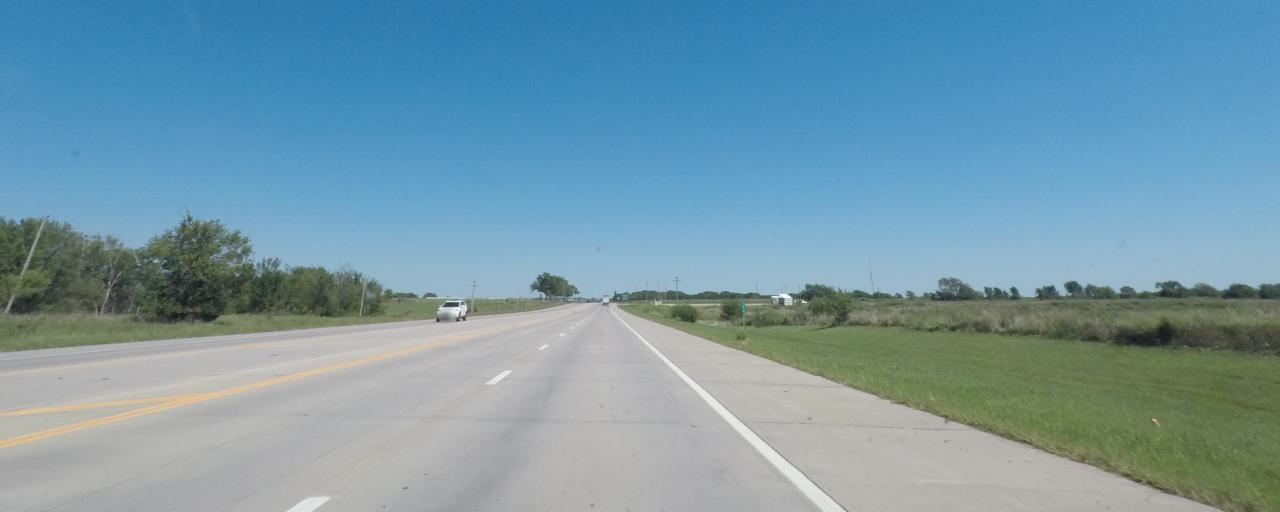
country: US
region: Kansas
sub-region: Lyon County
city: Emporia
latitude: 38.4123
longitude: -96.2574
